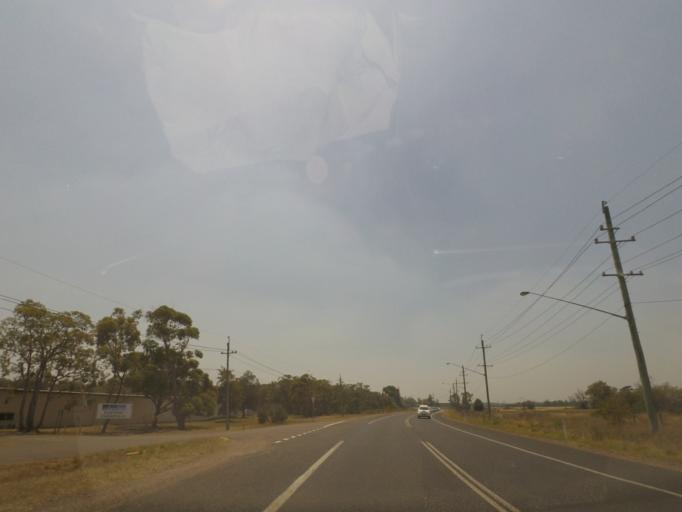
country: AU
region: New South Wales
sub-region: Newcastle
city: Mayfield West
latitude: -32.8274
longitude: 151.7346
